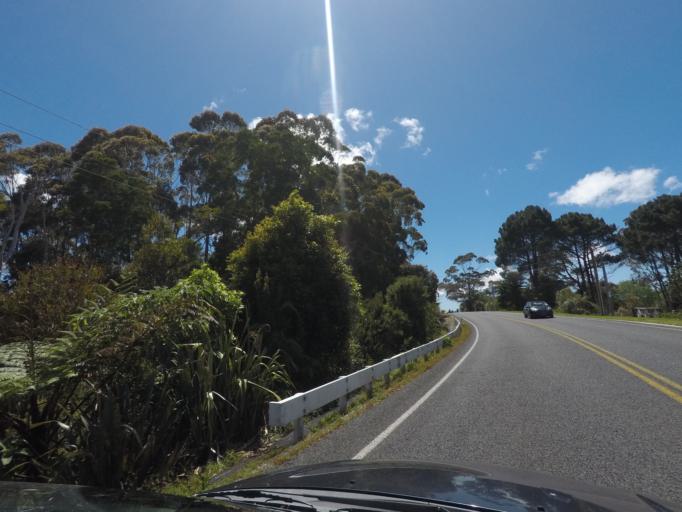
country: NZ
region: Auckland
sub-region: Auckland
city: Rothesay Bay
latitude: -36.7539
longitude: 174.6646
